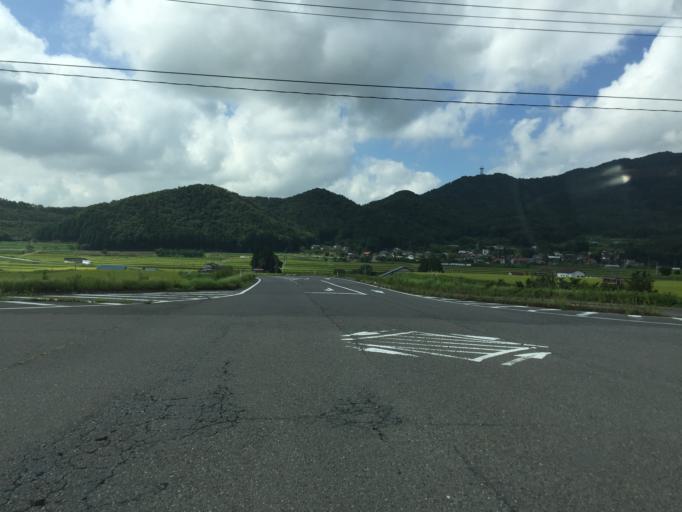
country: JP
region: Fukushima
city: Motomiya
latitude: 37.5238
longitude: 140.3741
